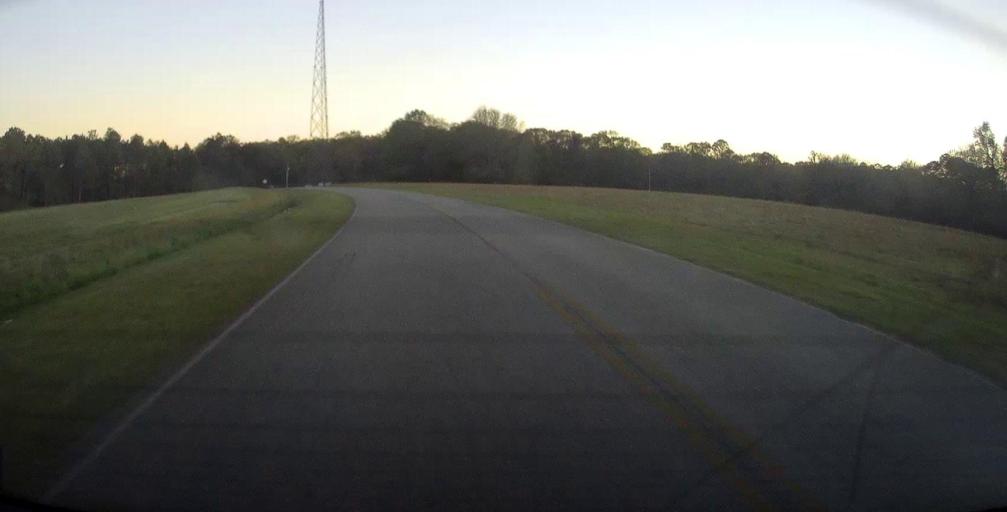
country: US
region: Georgia
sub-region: Crisp County
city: Cordele
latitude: 31.9535
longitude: -83.7535
